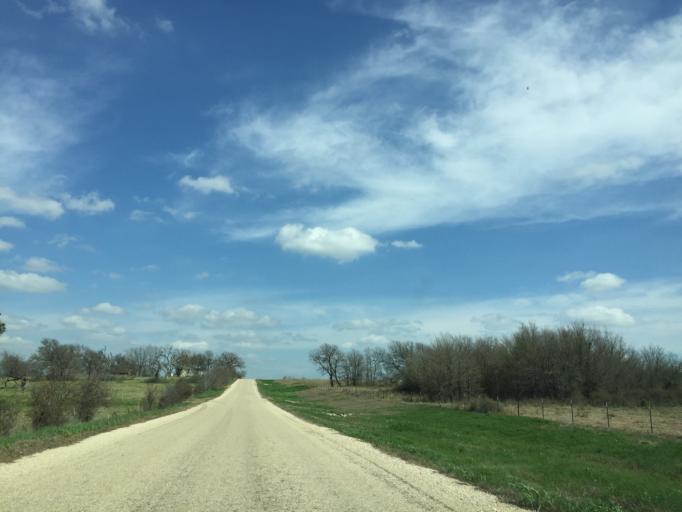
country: US
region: Texas
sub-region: Milam County
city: Thorndale
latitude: 30.5529
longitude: -97.2221
